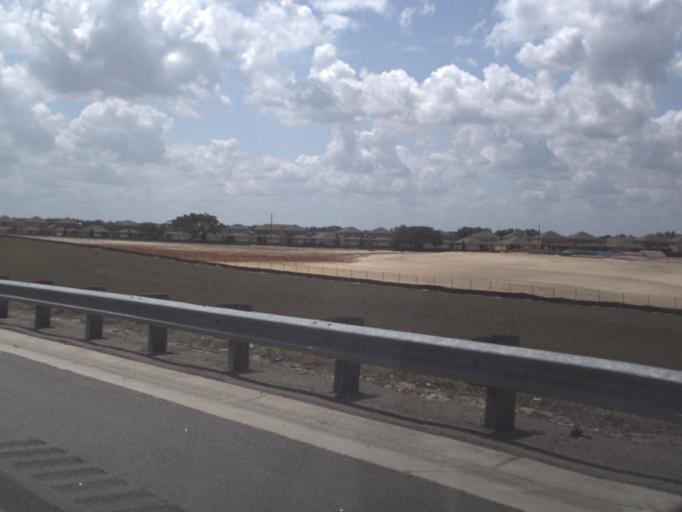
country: US
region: Florida
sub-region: Polk County
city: Citrus Ridge
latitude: 28.4411
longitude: -81.6408
